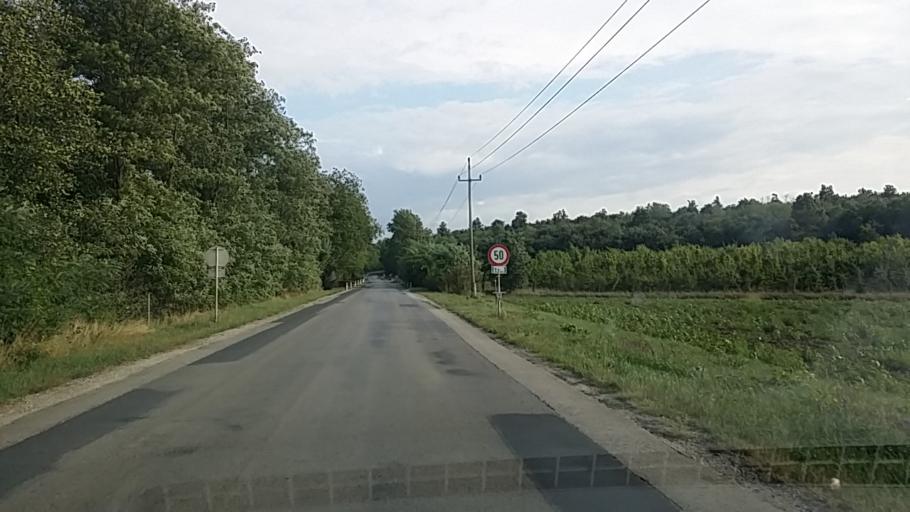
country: AT
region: Burgenland
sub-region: Eisenstadt-Umgebung
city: Sankt Margarethen im Burgenland
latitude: 47.7674
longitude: 16.6200
